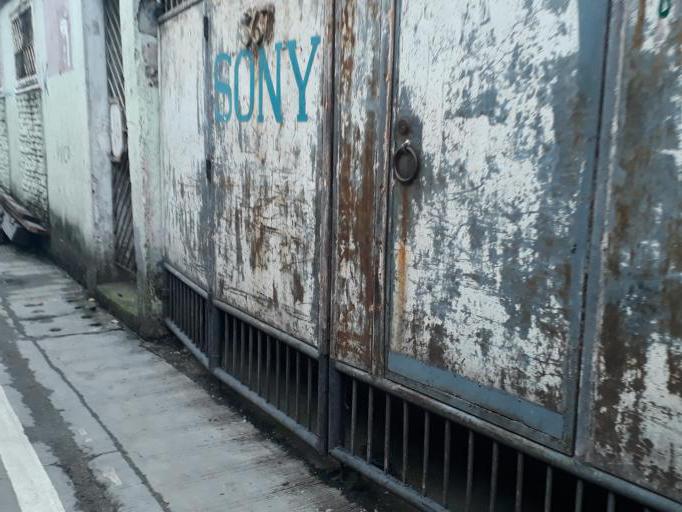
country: PH
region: Calabarzon
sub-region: Province of Rizal
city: Malabon
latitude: 14.6716
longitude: 120.9365
